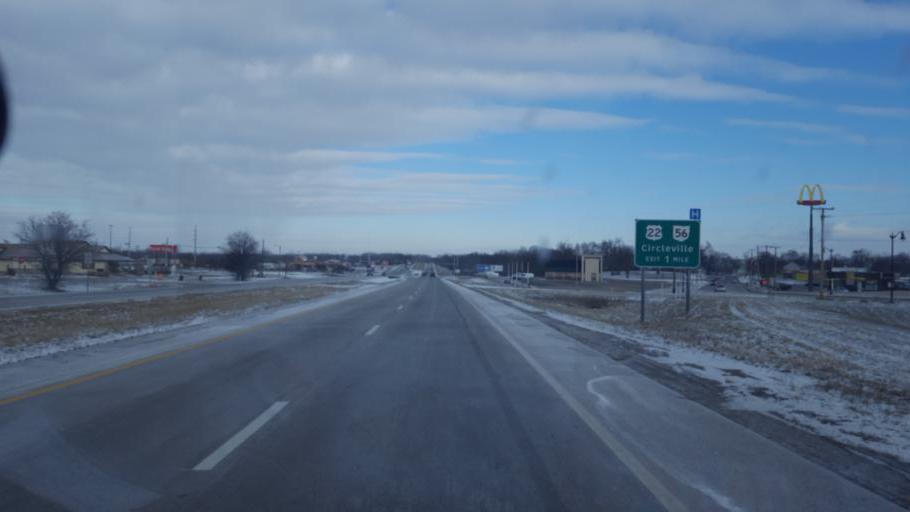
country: US
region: Ohio
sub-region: Pickaway County
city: Logan Elm Village
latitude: 39.5848
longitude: -82.9531
